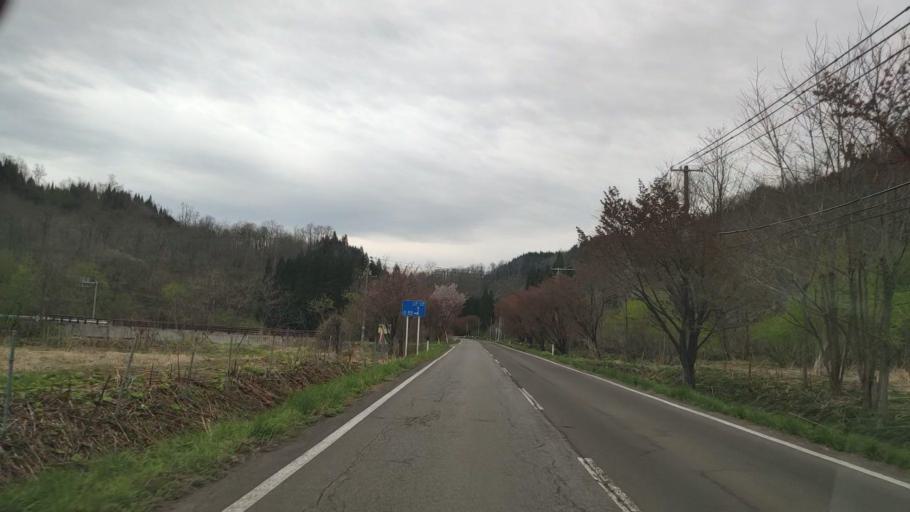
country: JP
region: Akita
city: Hanawa
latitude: 40.3540
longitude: 140.7793
